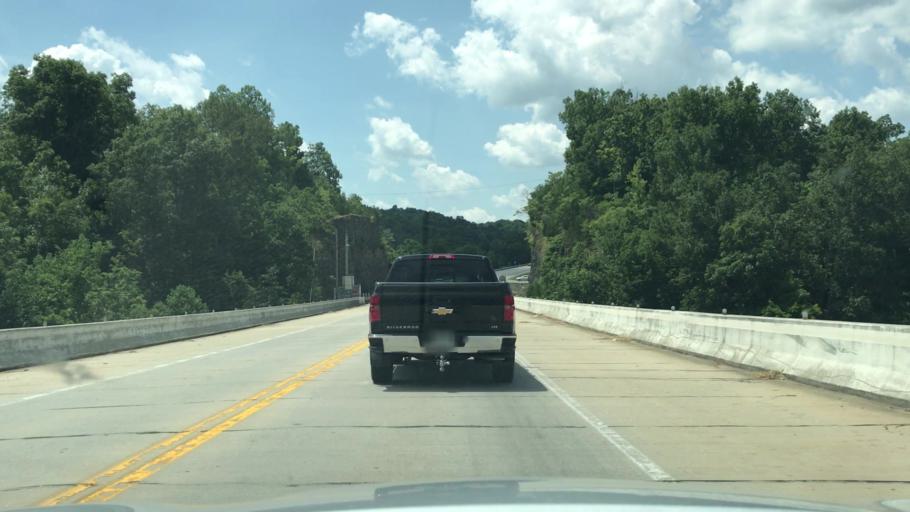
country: US
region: Tennessee
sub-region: Pickett County
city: Byrdstown
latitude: 36.5321
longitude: -85.1613
